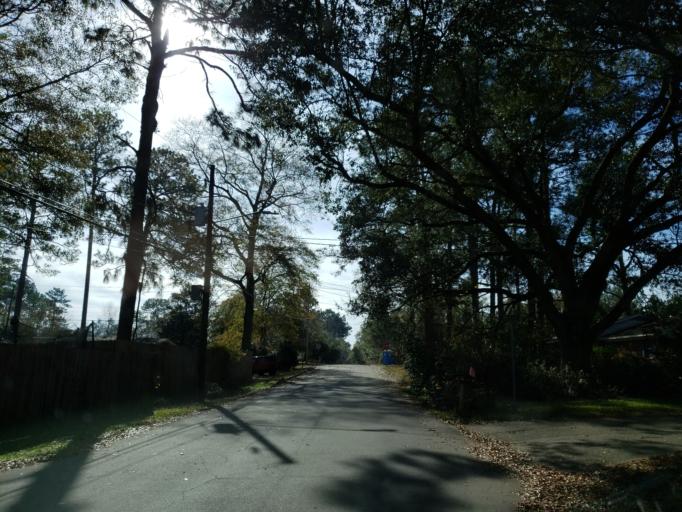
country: US
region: Mississippi
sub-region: Forrest County
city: Hattiesburg
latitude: 31.3107
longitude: -89.3269
